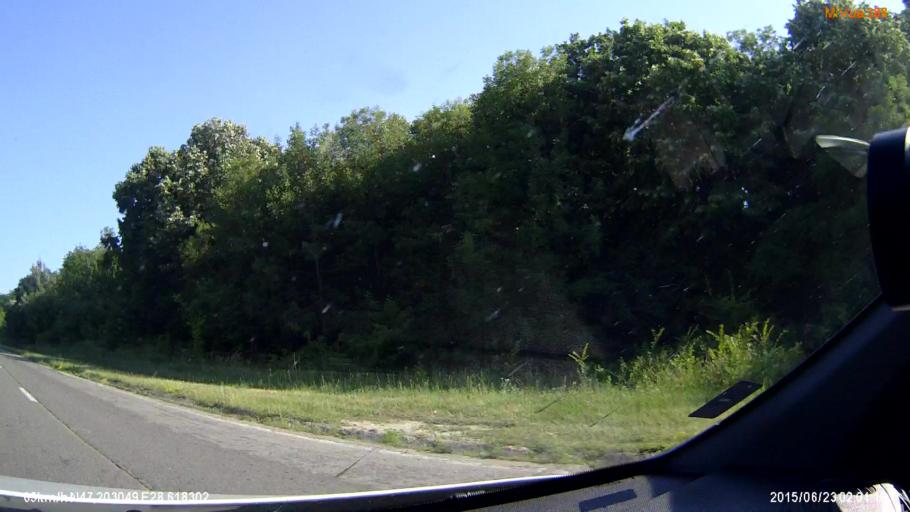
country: MD
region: Straseni
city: Straseni
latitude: 47.2033
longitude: 28.6180
